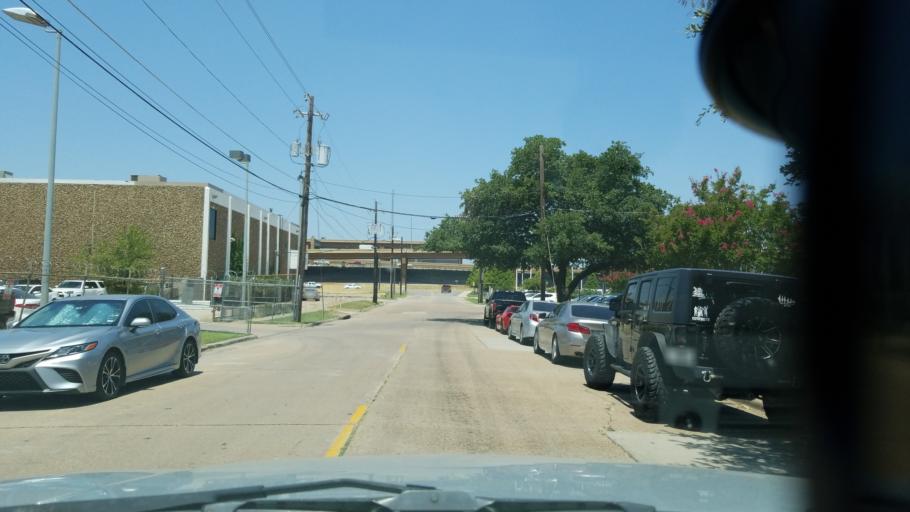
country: US
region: Texas
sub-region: Dallas County
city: Farmers Branch
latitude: 32.9066
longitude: -96.8903
